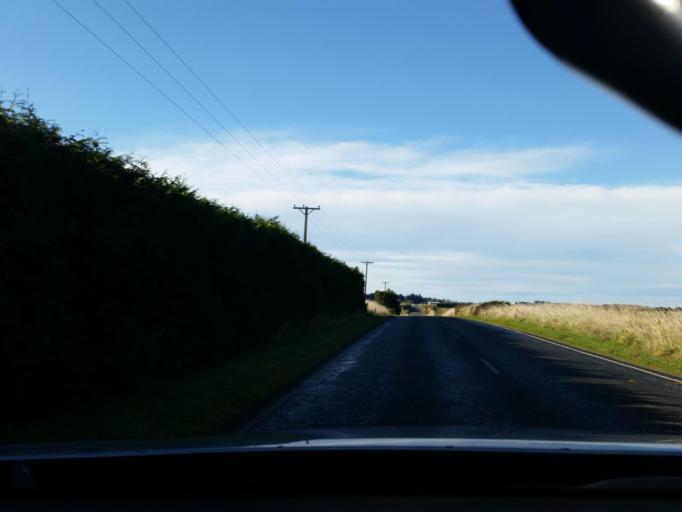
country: NZ
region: Southland
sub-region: Southland District
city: Riverton
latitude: -46.1544
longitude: 168.0482
